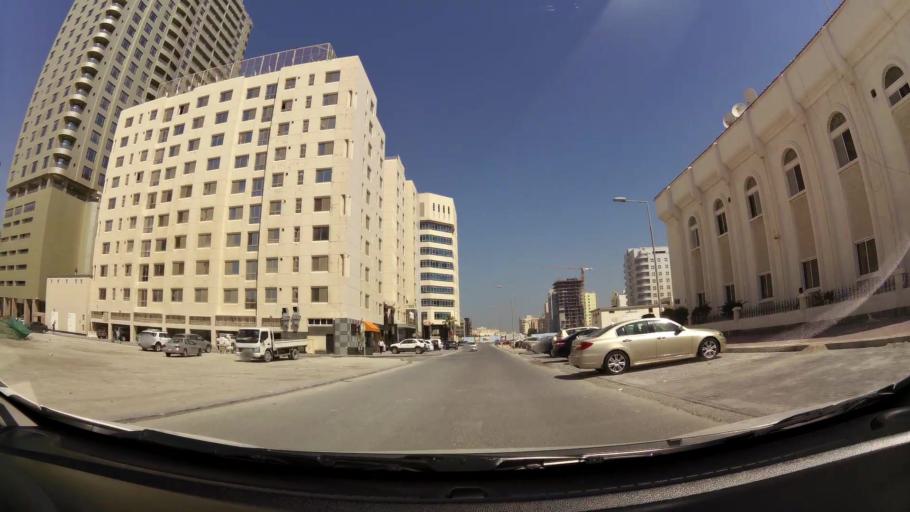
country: BH
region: Manama
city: Manama
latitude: 26.2138
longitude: 50.6002
